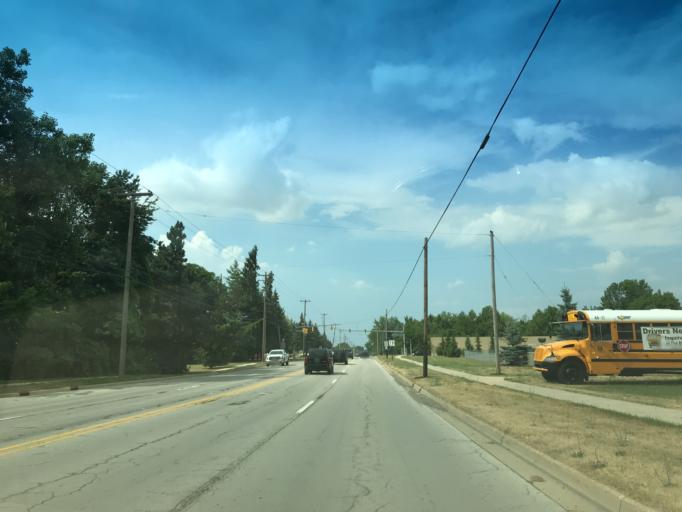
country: US
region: Michigan
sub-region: Eaton County
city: Waverly
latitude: 42.7322
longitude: -84.6620
